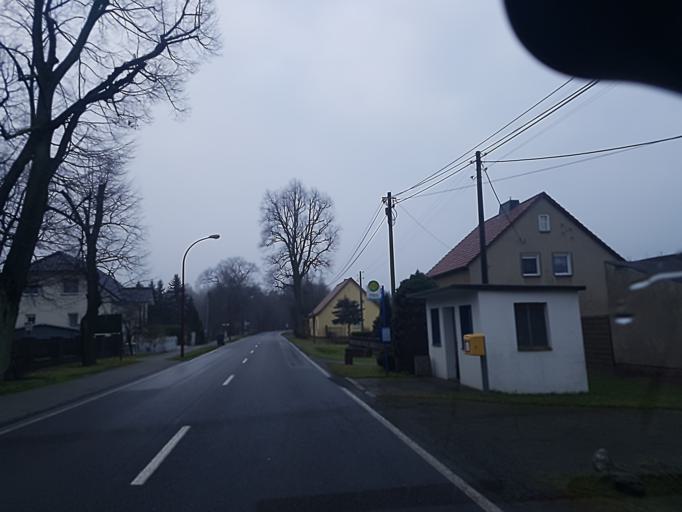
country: DE
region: Brandenburg
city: Finsterwalde
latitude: 51.5852
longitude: 13.7024
